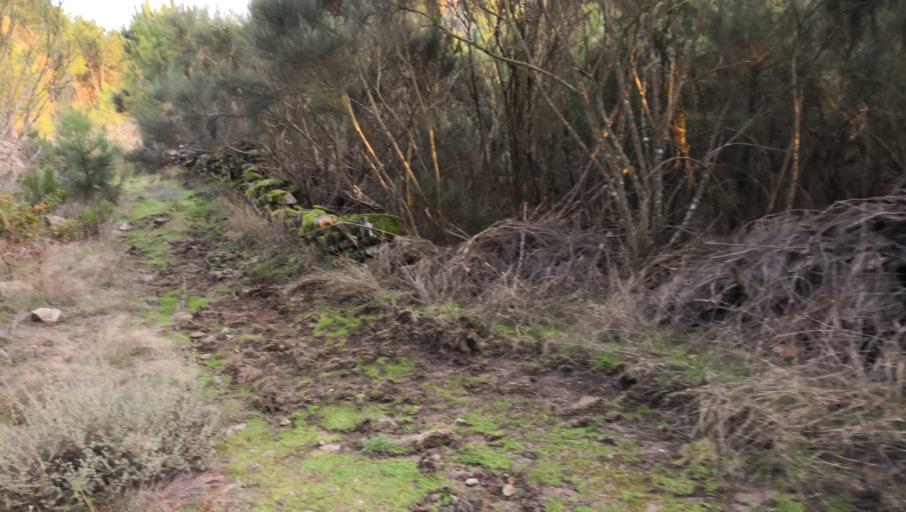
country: PT
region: Vila Real
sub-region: Vila Real
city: Vila Real
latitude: 41.3333
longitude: -7.7062
